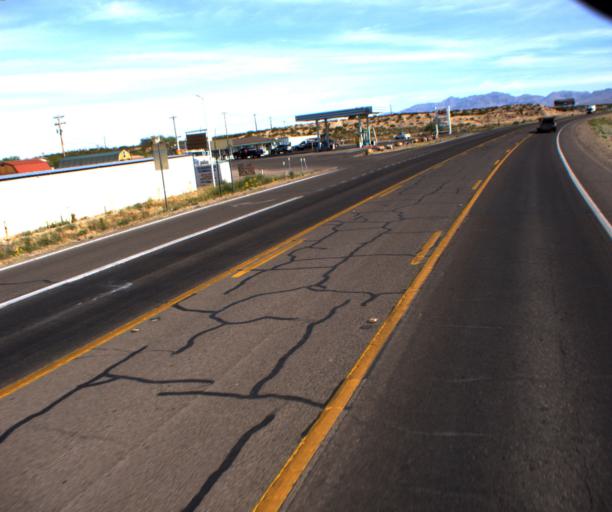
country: US
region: Arizona
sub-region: Graham County
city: Cactus Flat
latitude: 32.7792
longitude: -109.7157
